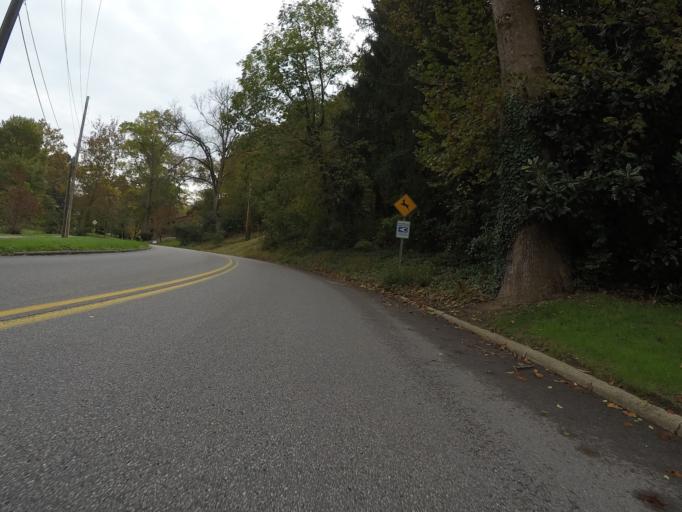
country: US
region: West Virginia
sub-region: Cabell County
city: Huntington
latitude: 38.4031
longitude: -82.4238
